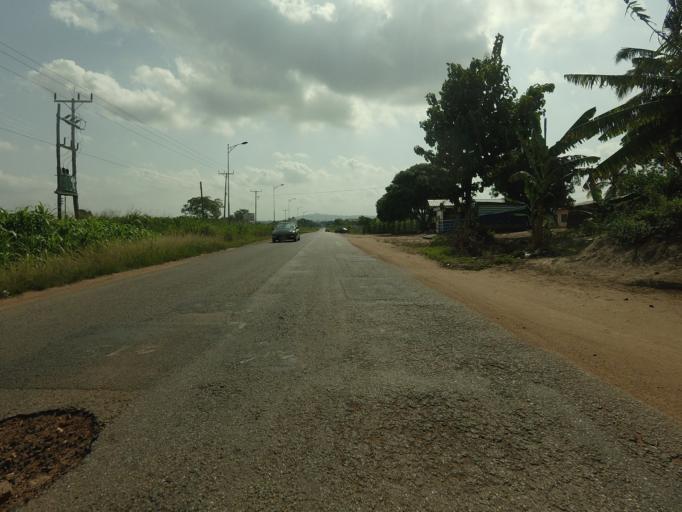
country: GH
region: Volta
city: Ho
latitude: 6.5983
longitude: 0.5154
